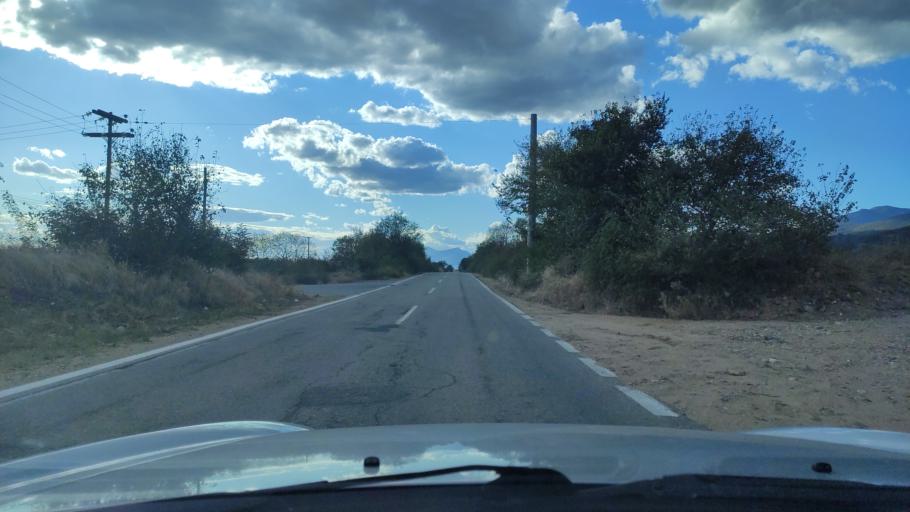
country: GR
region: East Macedonia and Thrace
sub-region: Nomos Rodopis
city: Iasmos
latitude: 41.1196
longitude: 25.0967
